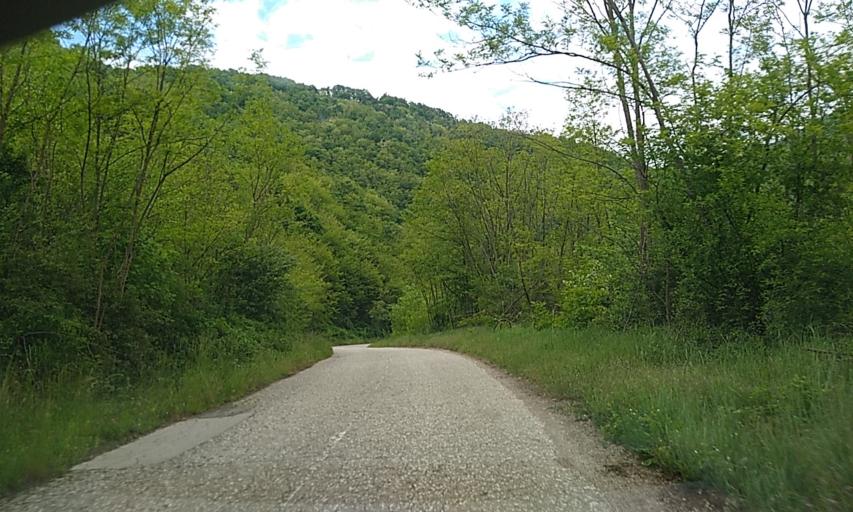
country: RS
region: Central Serbia
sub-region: Pcinjski Okrug
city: Vladicin Han
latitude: 42.7520
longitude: 22.0611
